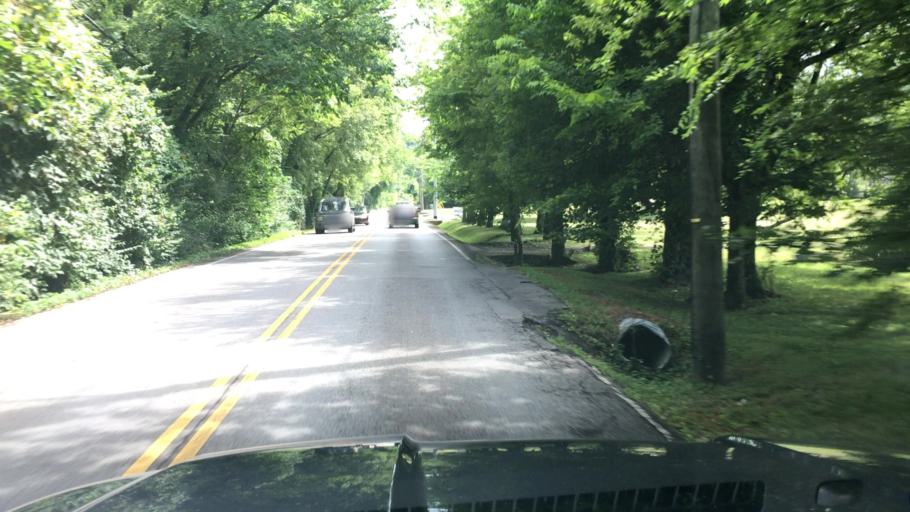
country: US
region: Tennessee
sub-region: Davidson County
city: Oak Hill
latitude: 36.0801
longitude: -86.8055
